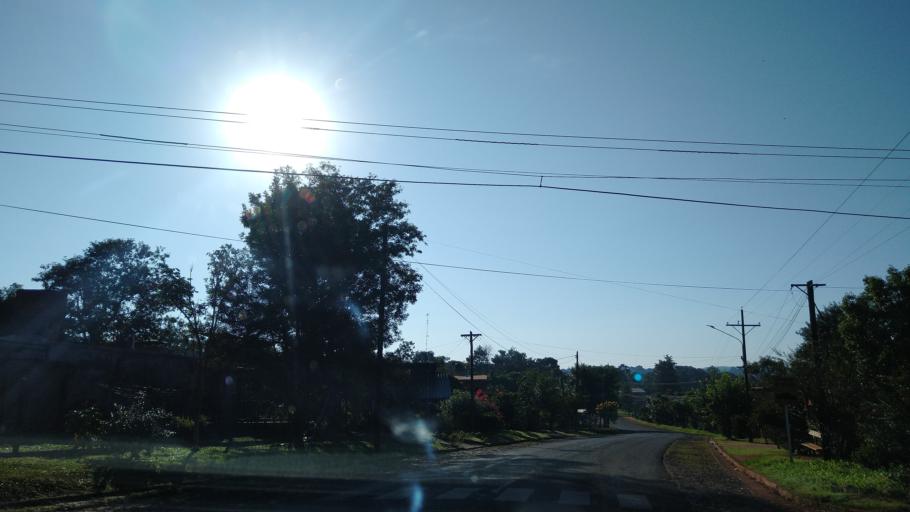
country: AR
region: Misiones
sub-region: Departamento de Montecarlo
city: Montecarlo
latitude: -26.5695
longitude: -54.7621
